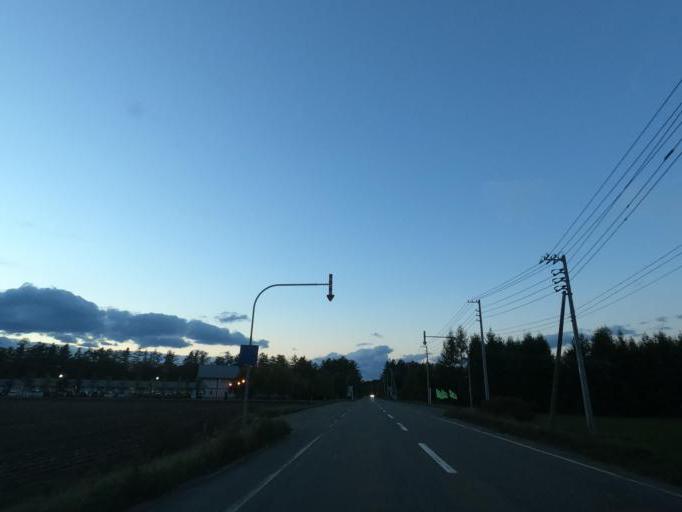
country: JP
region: Hokkaido
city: Obihiro
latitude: 42.6722
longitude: 143.1692
